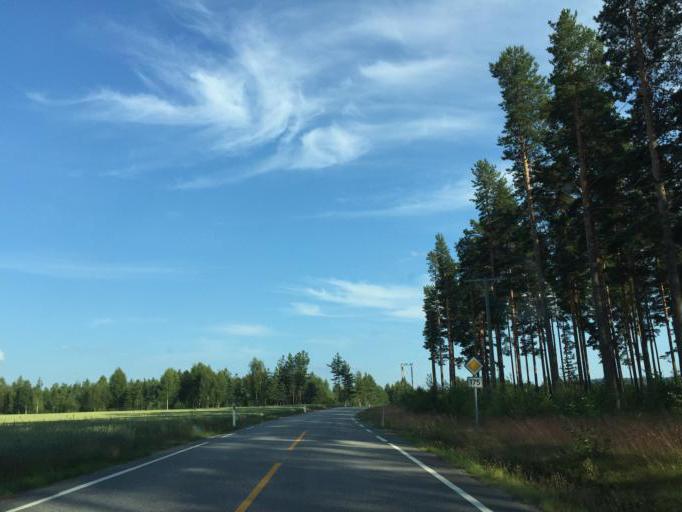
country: NO
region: Hedmark
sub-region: Kongsvinger
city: Spetalen
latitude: 60.2073
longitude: 11.8641
